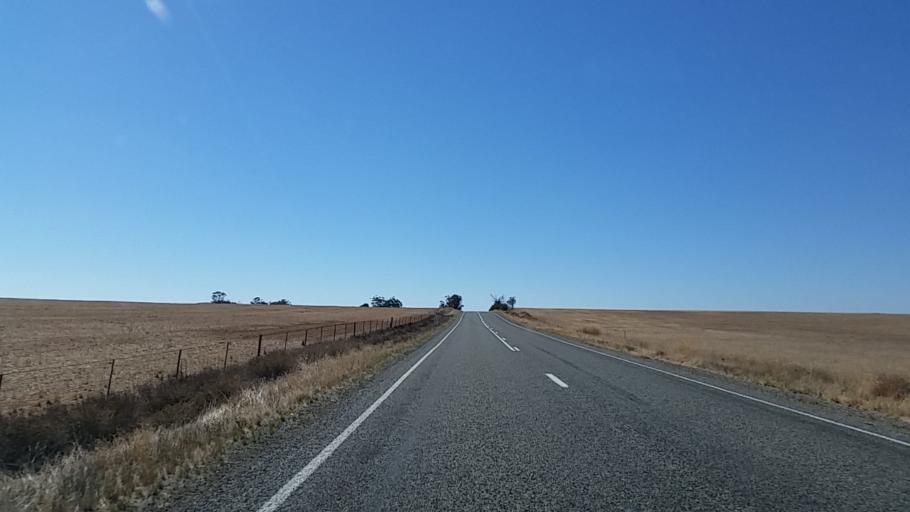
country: AU
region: South Australia
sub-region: Northern Areas
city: Jamestown
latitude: -33.3428
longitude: 138.8922
